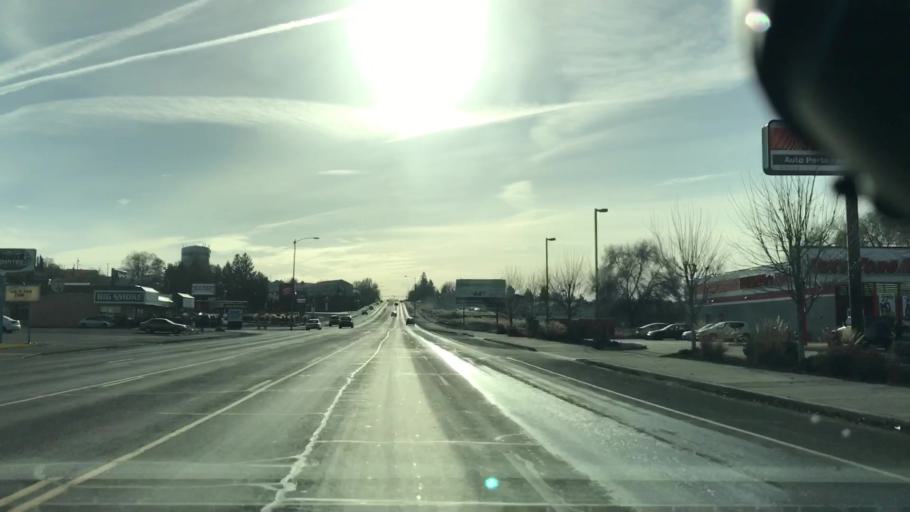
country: US
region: Washington
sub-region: Grant County
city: Moses Lake
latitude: 47.1293
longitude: -119.2696
